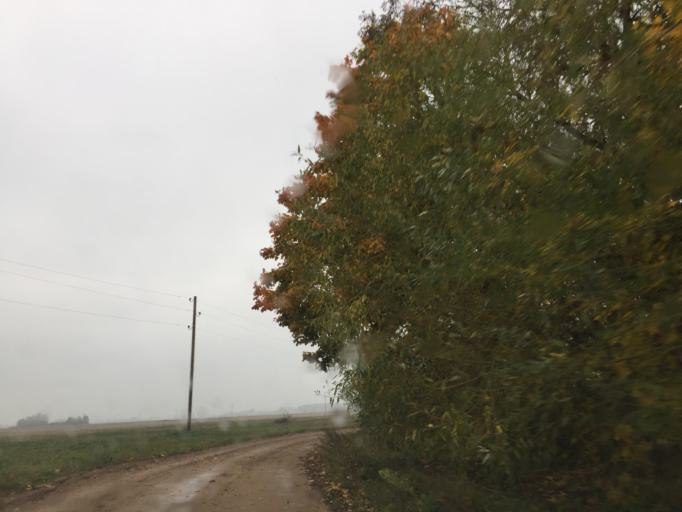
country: LV
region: Dobeles Rajons
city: Dobele
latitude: 56.6689
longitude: 23.4338
